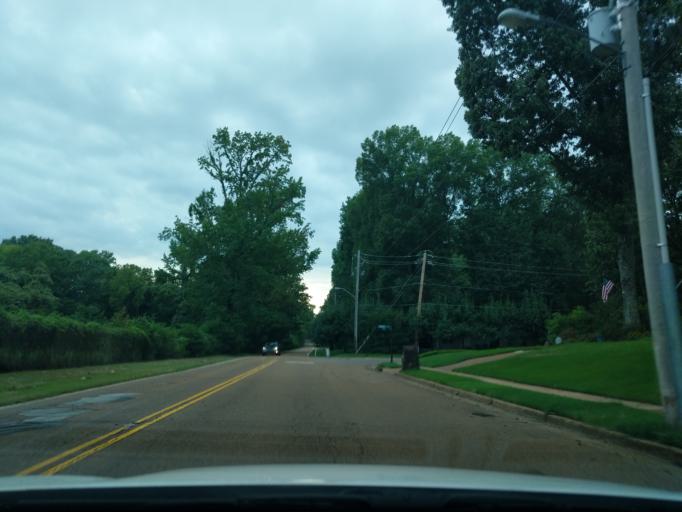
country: US
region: Tennessee
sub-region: Shelby County
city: Germantown
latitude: 35.0775
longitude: -89.8188
